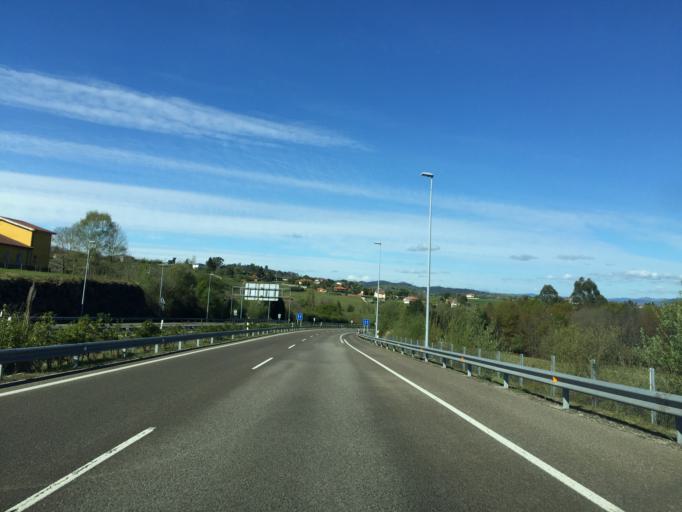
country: ES
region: Asturias
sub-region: Province of Asturias
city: Oviedo
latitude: 43.3478
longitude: -5.8996
